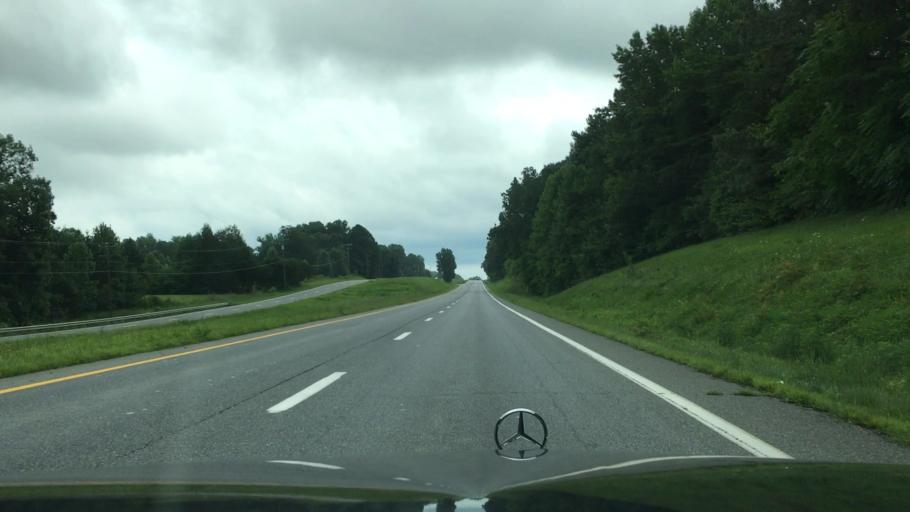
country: US
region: Virginia
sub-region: Appomattox County
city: Appomattox
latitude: 37.2819
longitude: -78.7076
